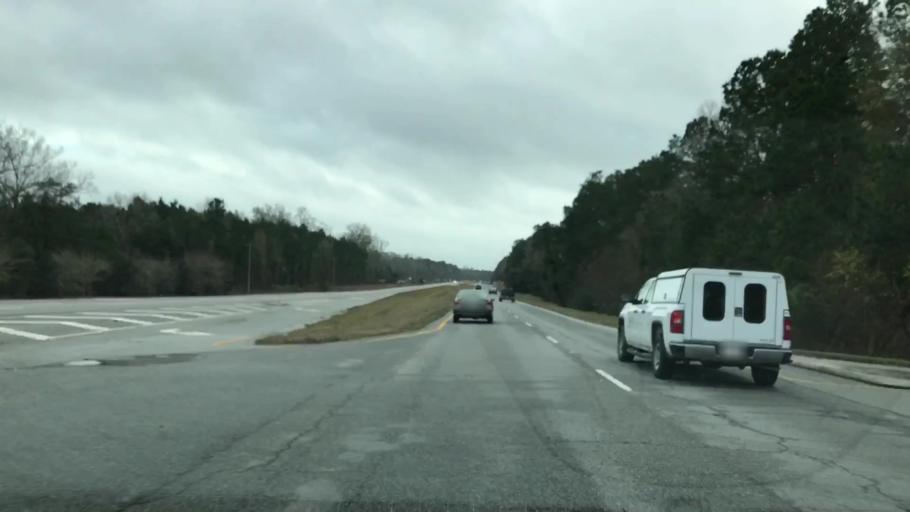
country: US
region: South Carolina
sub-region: Berkeley County
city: Moncks Corner
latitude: 33.1316
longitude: -80.0308
